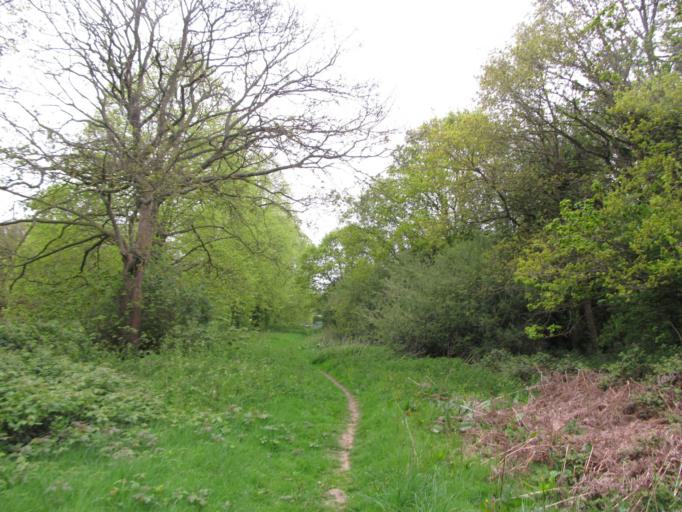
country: GB
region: England
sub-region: Royal Borough of Windsor and Maidenhead
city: Bisham
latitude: 51.5377
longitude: -0.7604
